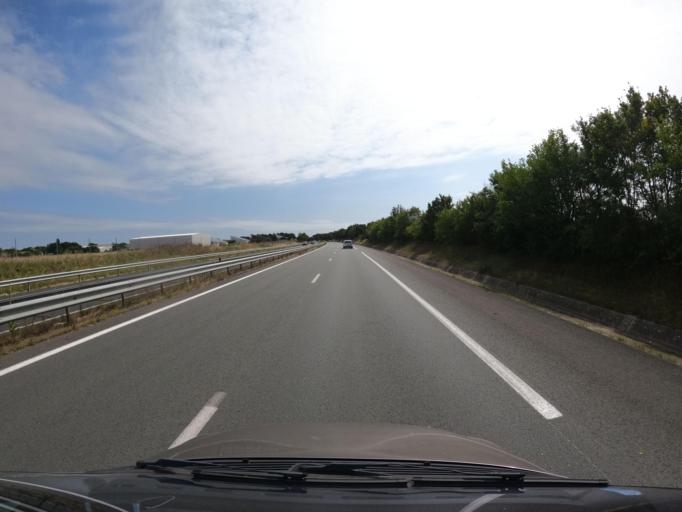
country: FR
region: Poitou-Charentes
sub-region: Departement de la Charente-Maritime
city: Courcon
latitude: 46.2238
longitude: -0.8557
